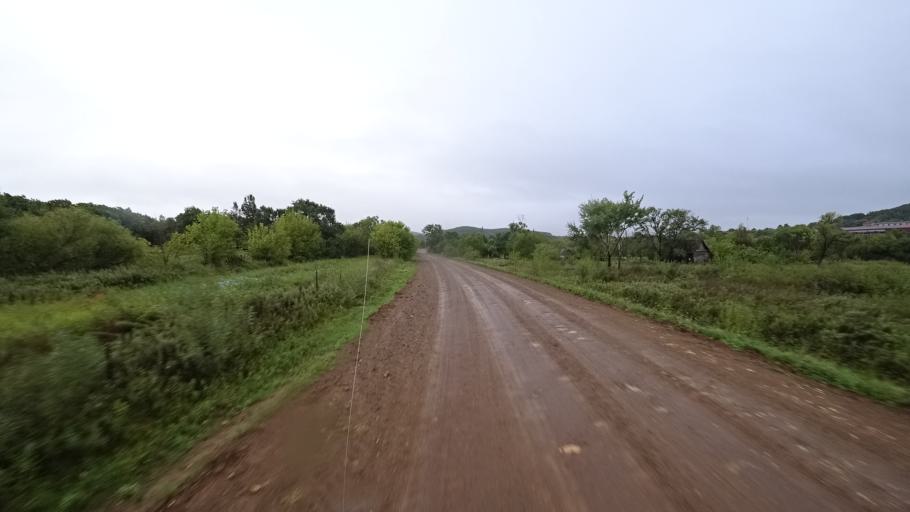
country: RU
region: Primorskiy
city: Monastyrishche
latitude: 44.2727
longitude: 132.4617
